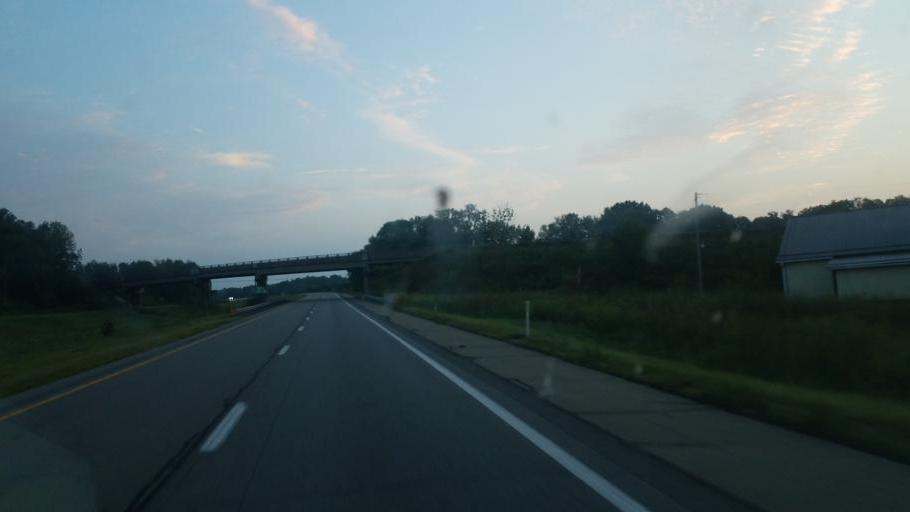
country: US
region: Pennsylvania
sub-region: Mercer County
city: Stoneboro
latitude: 41.4413
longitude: -80.1610
